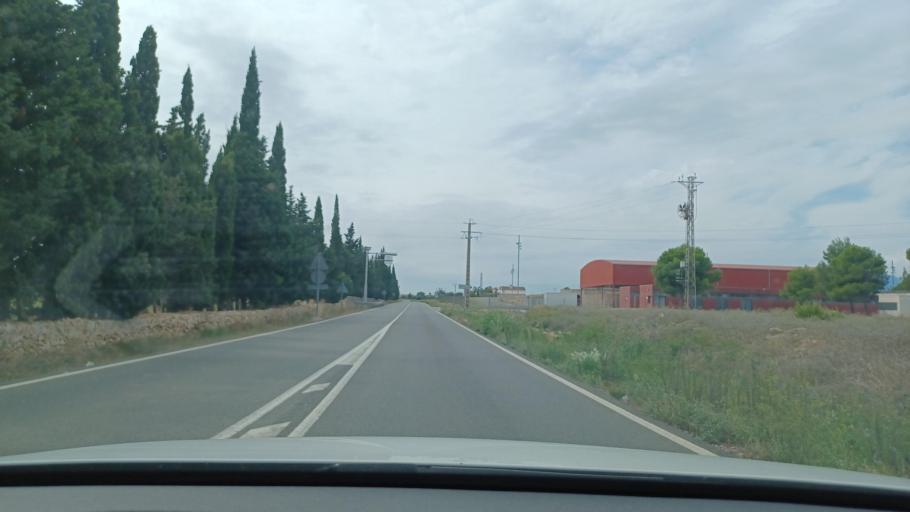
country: ES
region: Catalonia
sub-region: Provincia de Tarragona
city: Tortosa
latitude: 40.7716
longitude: 0.5122
